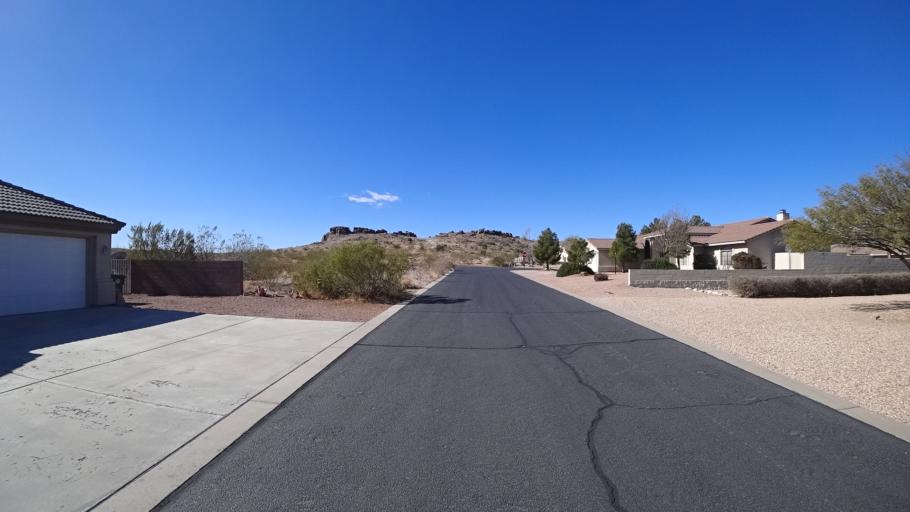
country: US
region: Arizona
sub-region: Mohave County
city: Kingman
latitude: 35.1873
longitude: -114.0252
